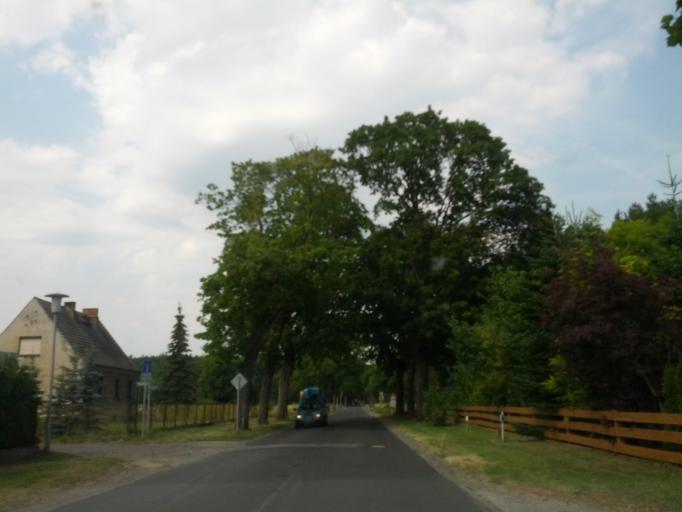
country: DE
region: Brandenburg
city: Nauen
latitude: 52.6887
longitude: 12.9361
